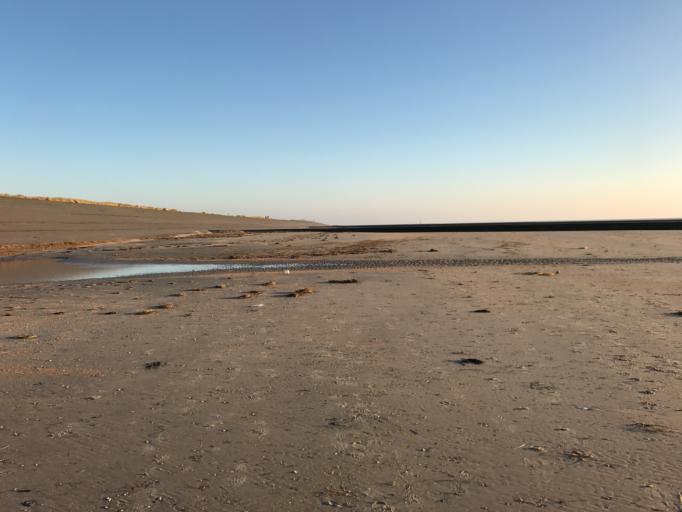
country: DE
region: Lower Saxony
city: Borkum
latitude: 53.5703
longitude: 6.6878
